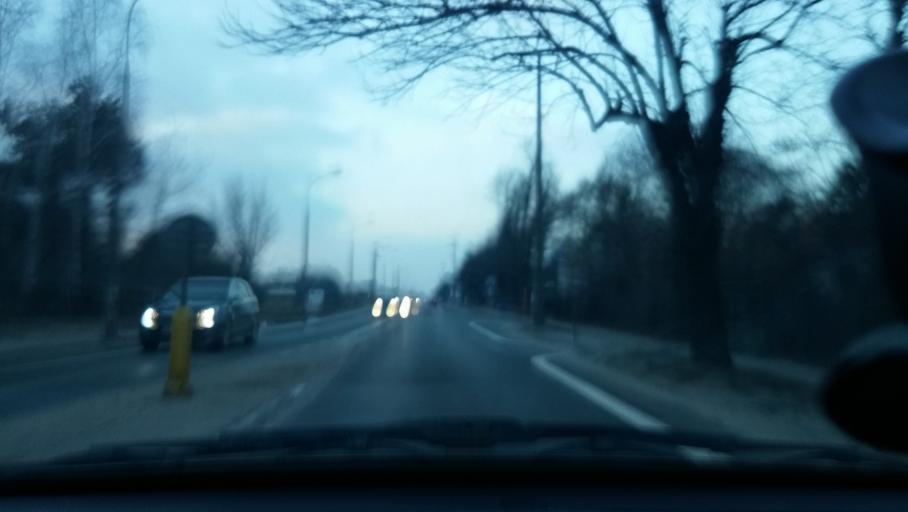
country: PL
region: Masovian Voivodeship
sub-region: Warszawa
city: Wawer
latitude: 52.1884
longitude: 21.1850
